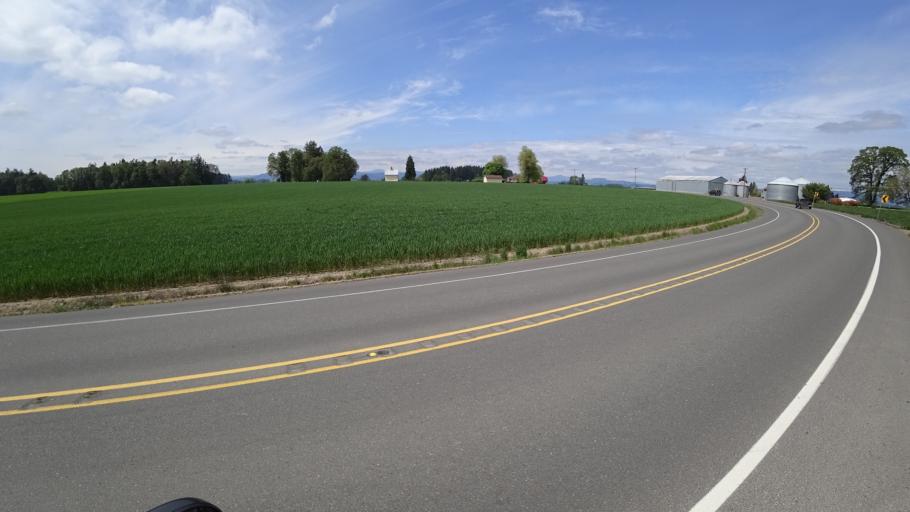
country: US
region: Oregon
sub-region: Washington County
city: North Plains
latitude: 45.5614
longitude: -122.9994
